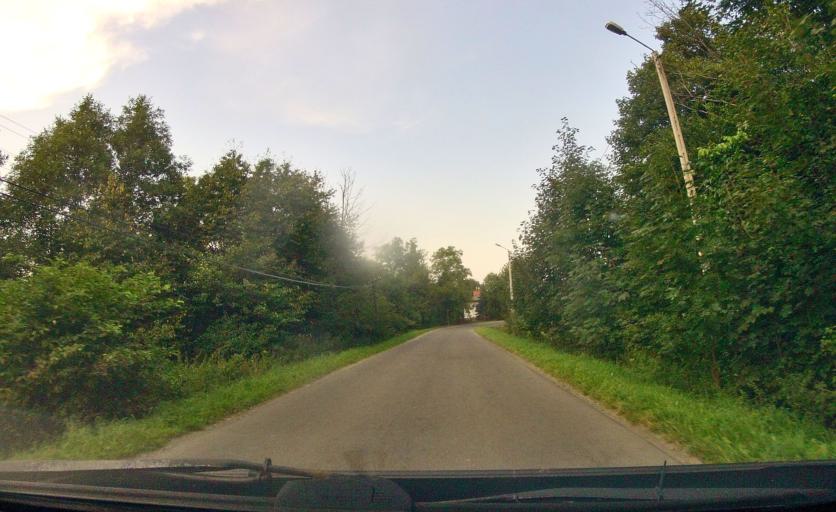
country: PL
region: Subcarpathian Voivodeship
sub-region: Powiat krosnienski
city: Dukla
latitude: 49.5523
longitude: 21.6215
